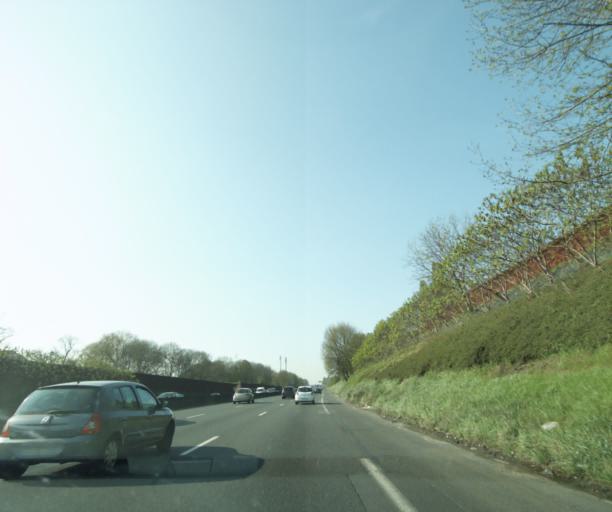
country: FR
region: Ile-de-France
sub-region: Departement de l'Essonne
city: Villemoisson-sur-Orge
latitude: 48.6819
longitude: 2.3304
